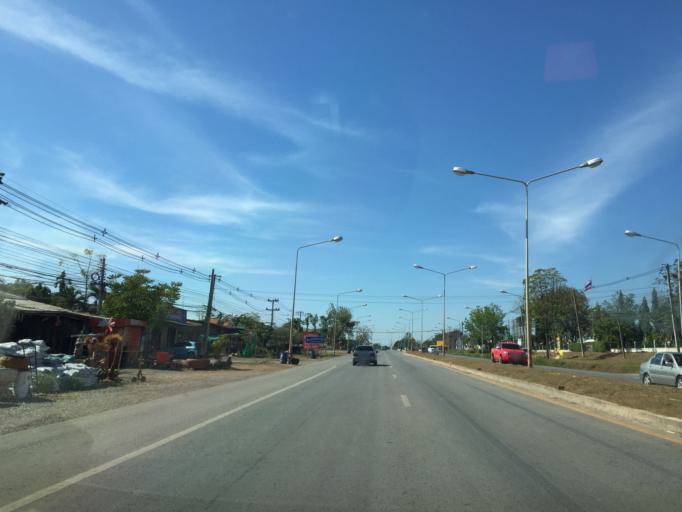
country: TH
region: Changwat Nong Bua Lamphu
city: Na Klang
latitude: 17.3055
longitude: 102.1897
